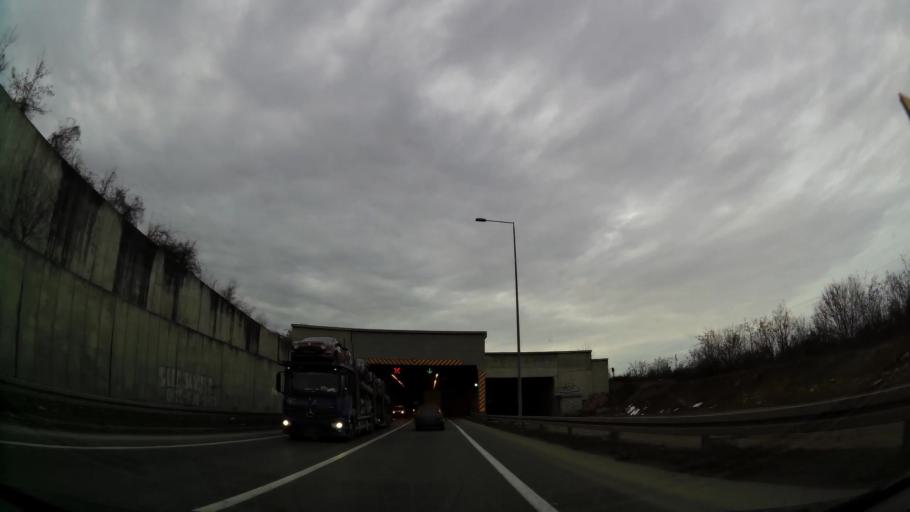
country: RS
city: Ostruznica
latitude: 44.7272
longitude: 20.3519
